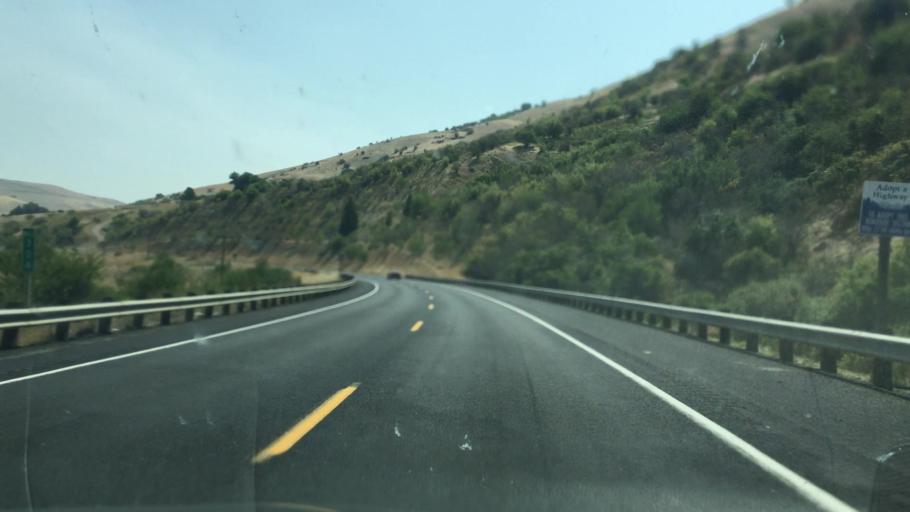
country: US
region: Idaho
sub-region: Nez Perce County
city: Lapwai
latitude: 46.4413
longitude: -116.8423
